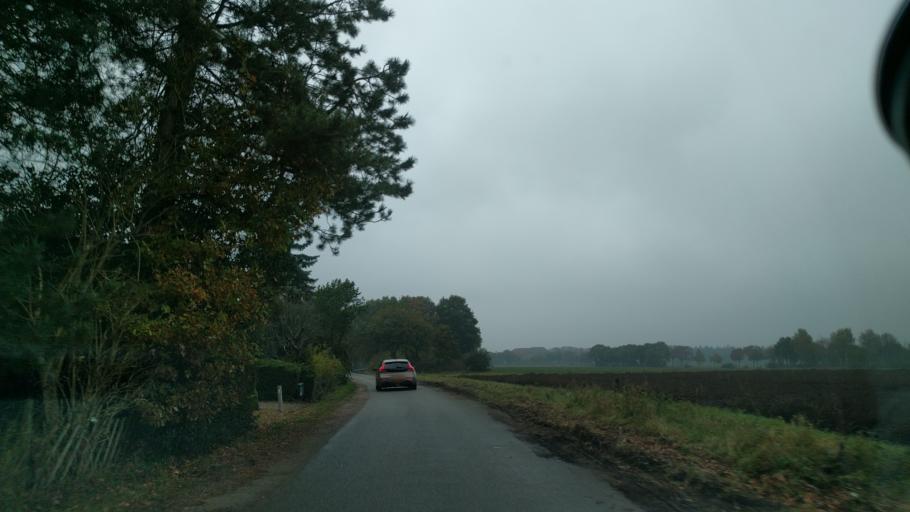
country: NL
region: North Brabant
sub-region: Gemeente Rucphen
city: Rucphen
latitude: 51.5363
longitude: 4.5482
